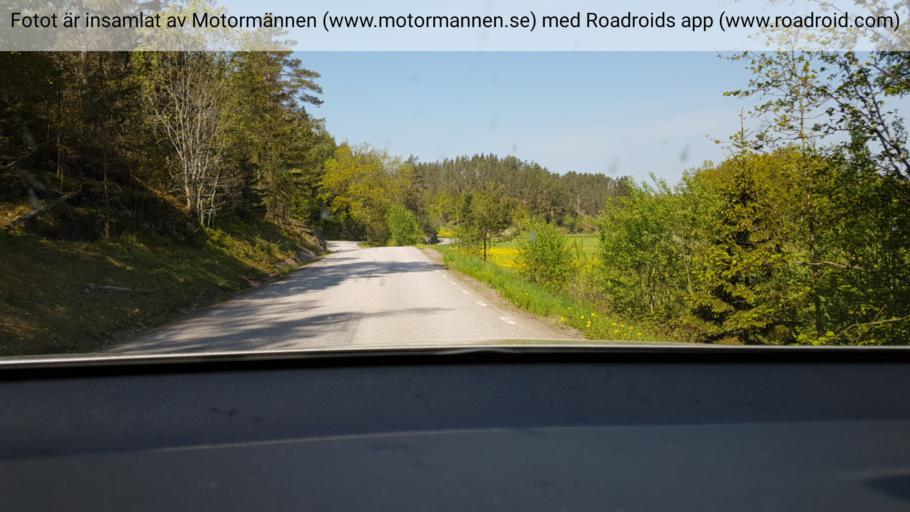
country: SE
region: Kalmar
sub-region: Vasterviks Kommun
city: Vaestervik
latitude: 57.8302
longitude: 16.5500
